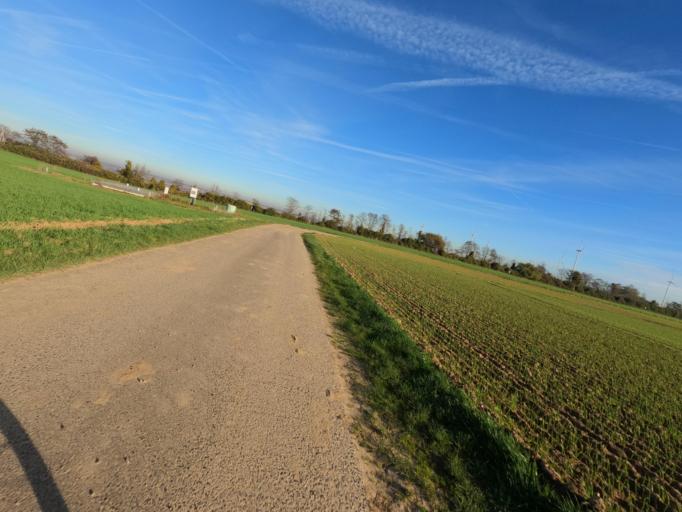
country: DE
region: North Rhine-Westphalia
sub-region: Regierungsbezirk Koln
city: Titz
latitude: 51.0370
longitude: 6.4743
